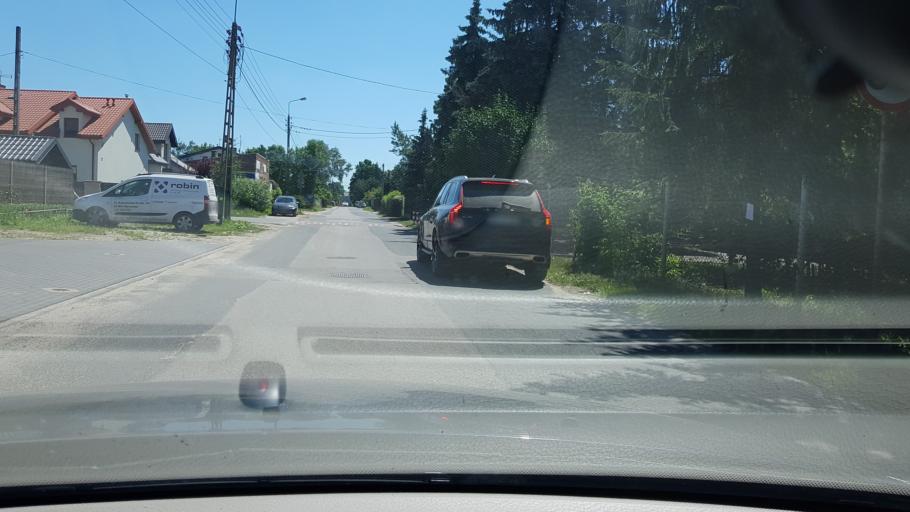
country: PL
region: Masovian Voivodeship
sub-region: Powiat wolominski
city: Marki
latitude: 52.3138
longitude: 21.1013
